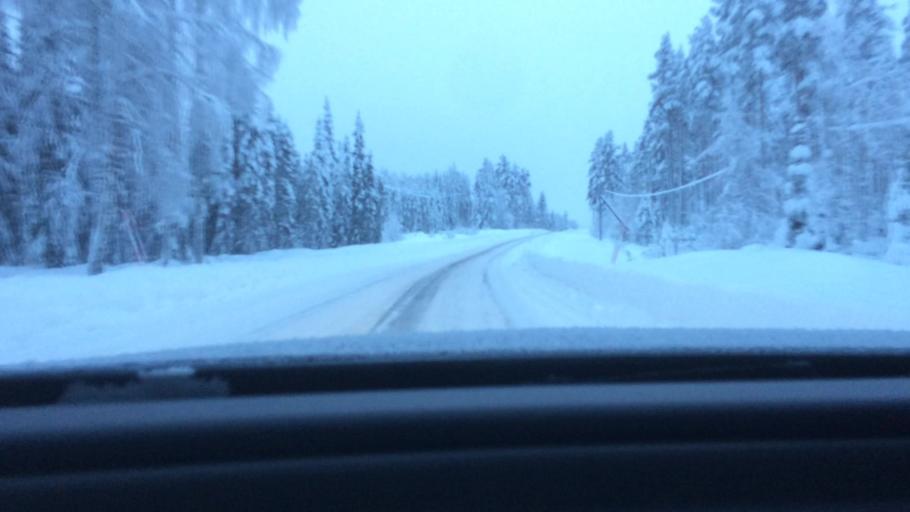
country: SE
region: Gaevleborg
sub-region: Ljusdals Kommun
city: Farila
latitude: 61.7679
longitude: 15.1623
